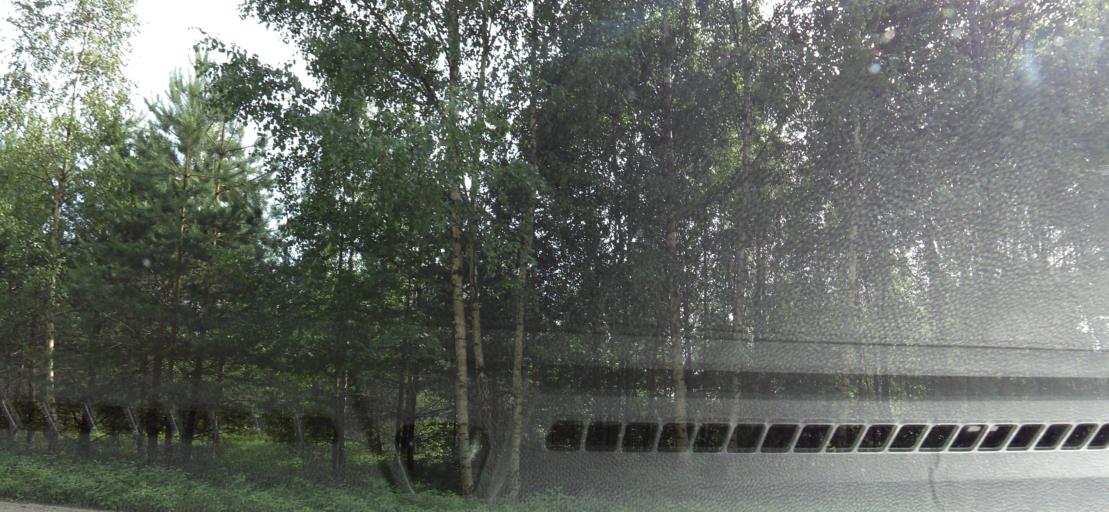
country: LT
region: Panevezys
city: Pasvalys
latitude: 55.9664
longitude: 24.3049
